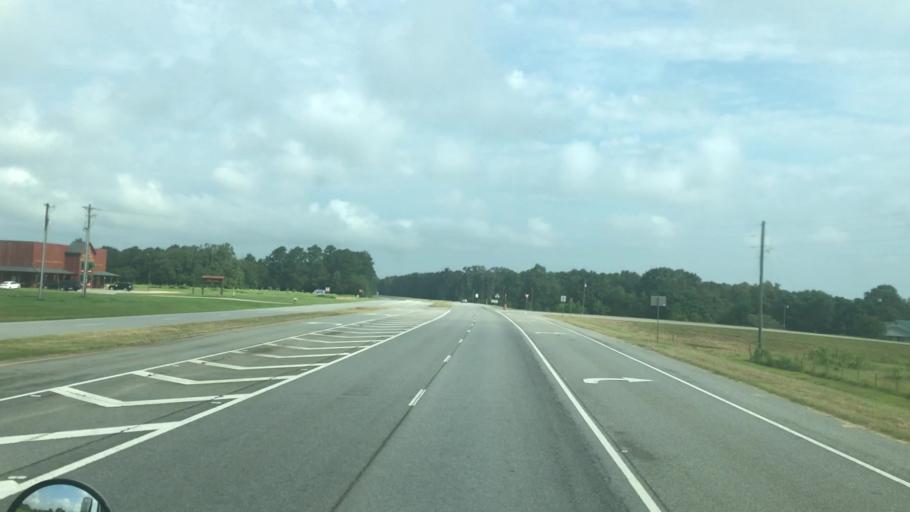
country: US
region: Georgia
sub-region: Miller County
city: Colquitt
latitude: 31.2392
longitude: -84.7873
